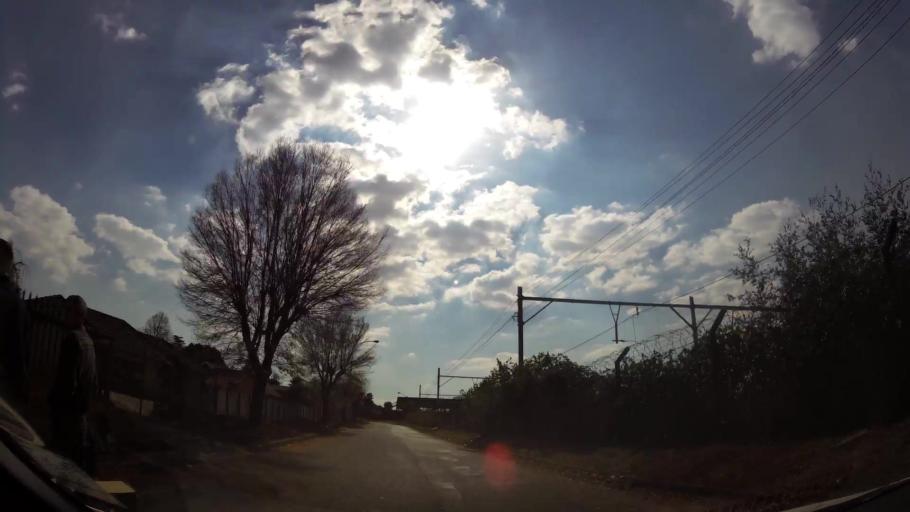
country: ZA
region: Gauteng
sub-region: Ekurhuleni Metropolitan Municipality
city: Germiston
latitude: -26.1827
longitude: 28.1990
